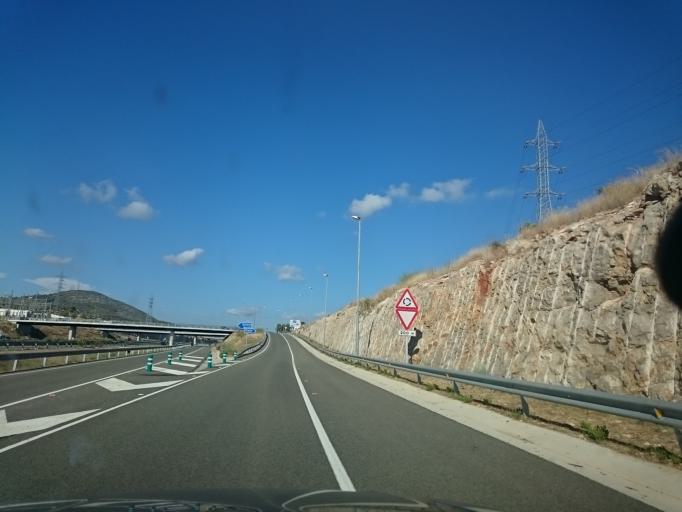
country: ES
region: Catalonia
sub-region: Provincia de Barcelona
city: Vilanova i la Geltru
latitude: 41.2513
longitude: 1.7152
